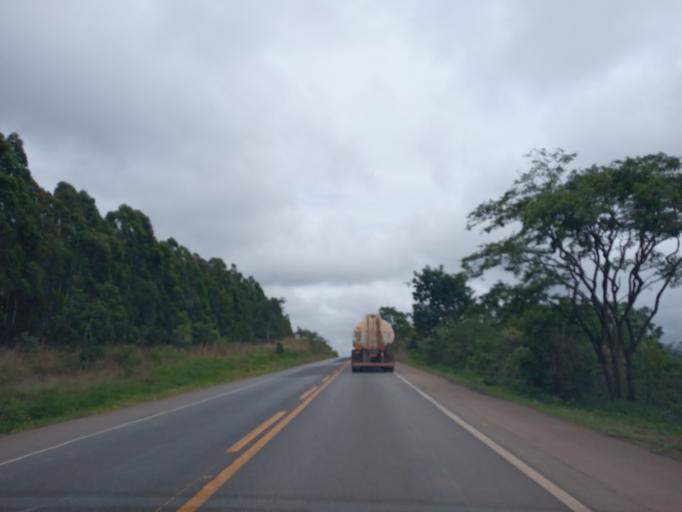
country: BR
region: Minas Gerais
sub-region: Campos Altos
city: Campos Altos
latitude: -19.5982
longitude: -46.2909
